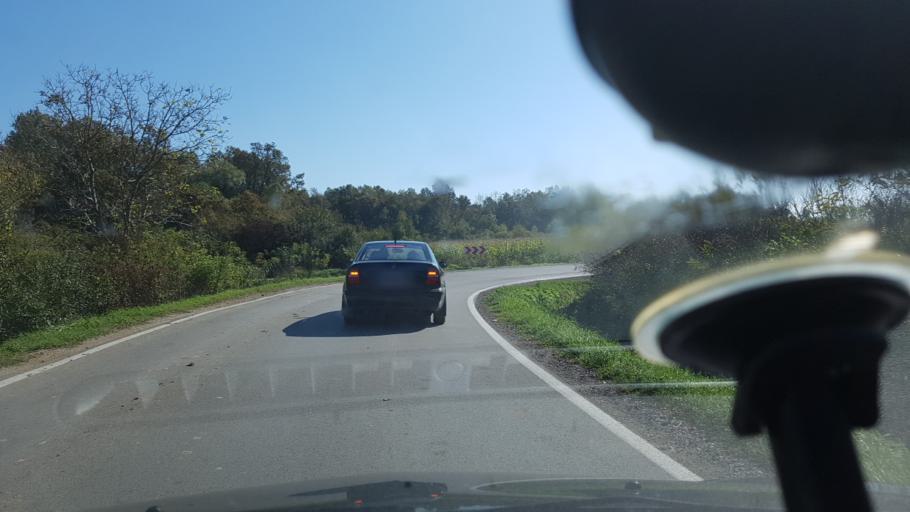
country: HR
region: Zagrebacka
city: Lupoglav
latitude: 45.7328
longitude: 16.3027
